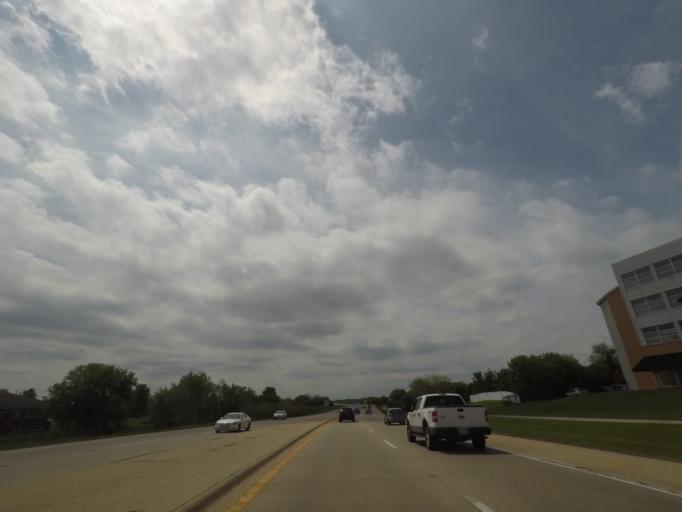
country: US
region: Illinois
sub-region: Winnebago County
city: Machesney Park
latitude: 42.3028
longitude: -88.9794
